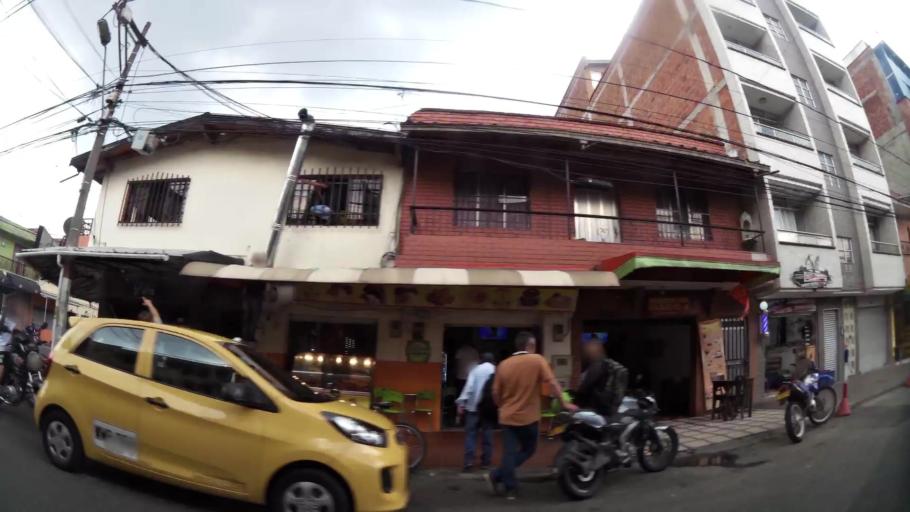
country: CO
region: Antioquia
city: Envigado
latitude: 6.1776
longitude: -75.5981
